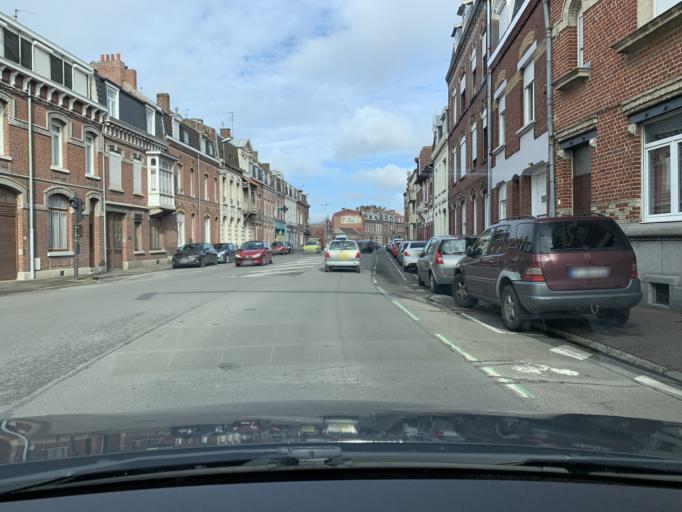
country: FR
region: Nord-Pas-de-Calais
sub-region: Departement du Nord
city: Douai
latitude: 50.3608
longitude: 3.0788
